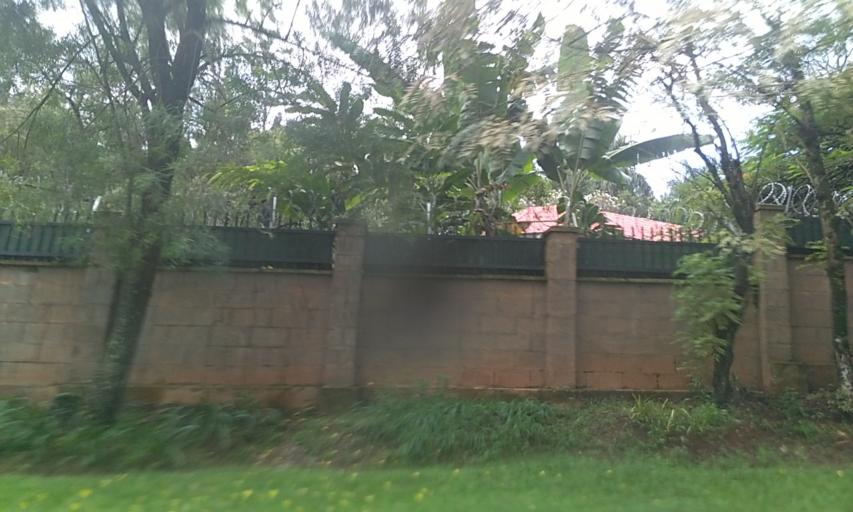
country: UG
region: Central Region
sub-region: Kampala District
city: Kampala
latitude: 0.3348
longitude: 32.5997
